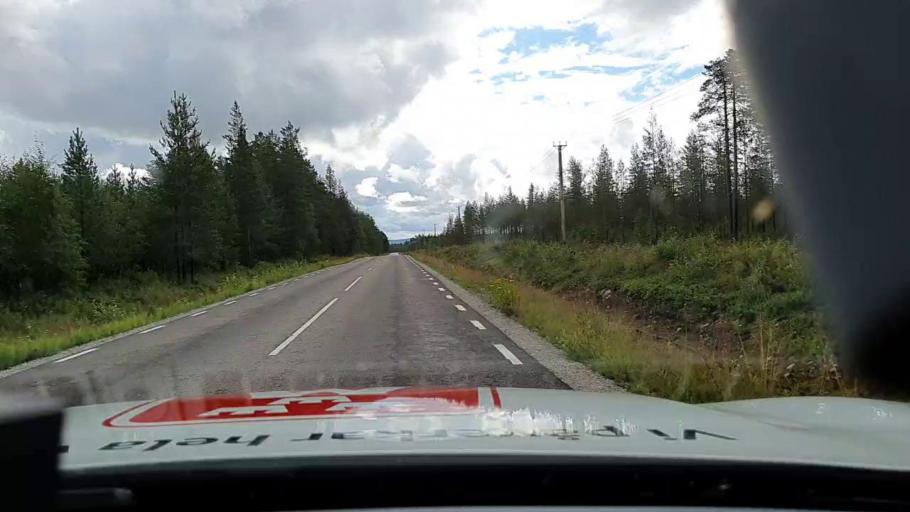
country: SE
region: Norrbotten
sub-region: Overkalix Kommun
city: OEverkalix
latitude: 66.2562
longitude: 22.8619
